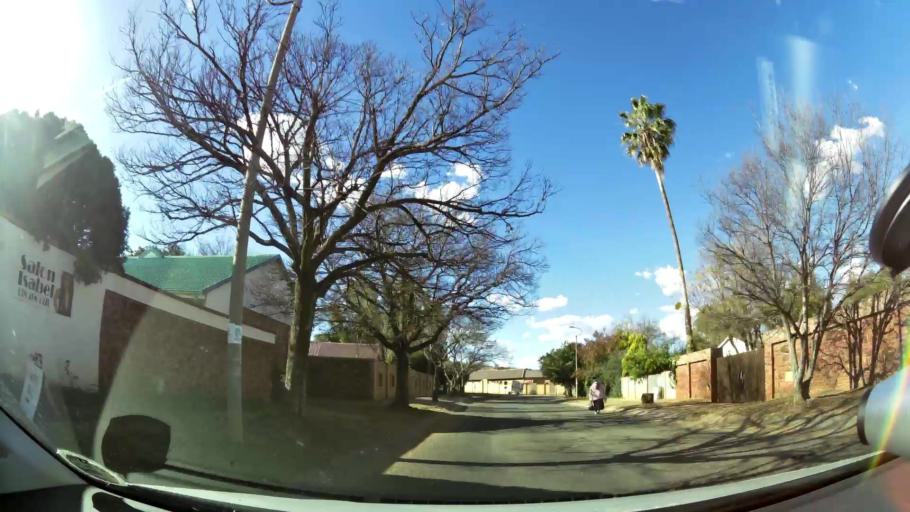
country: ZA
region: North-West
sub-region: Dr Kenneth Kaunda District Municipality
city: Klerksdorp
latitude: -26.8252
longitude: 26.6777
